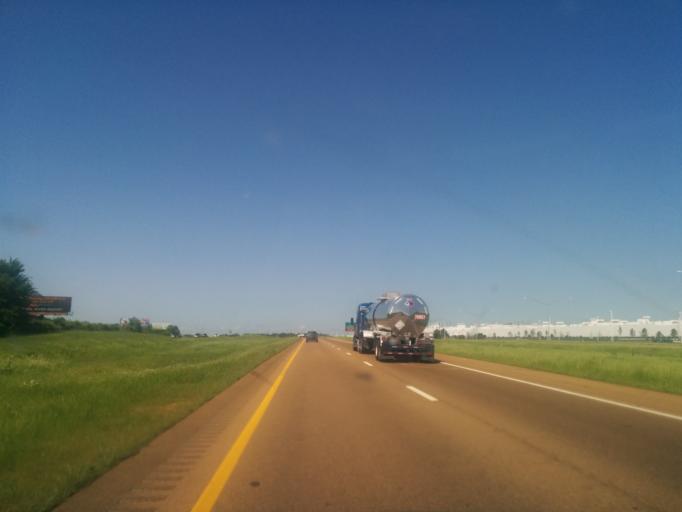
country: US
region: Mississippi
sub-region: Madison County
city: Canton
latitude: 32.5663
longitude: -90.0775
